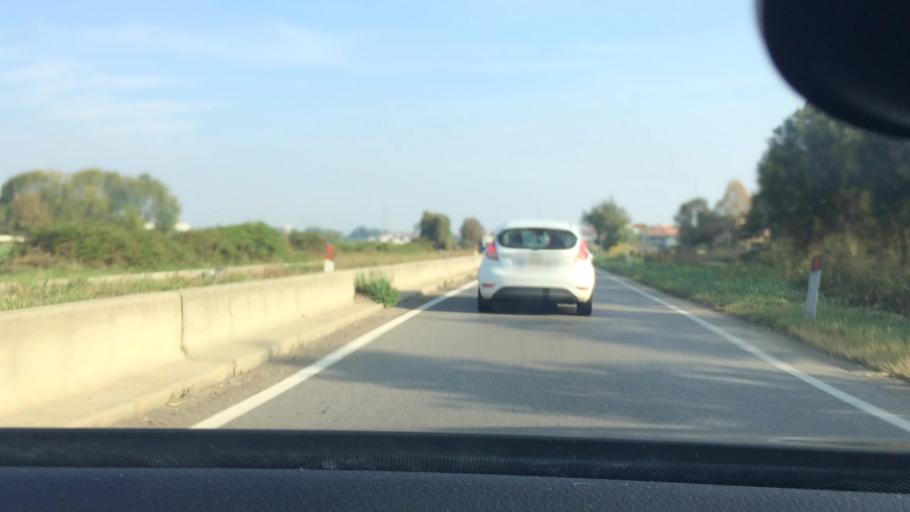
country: IT
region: Lombardy
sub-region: Citta metropolitana di Milano
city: San Giorgio Su Legnano
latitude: 45.5730
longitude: 8.9012
